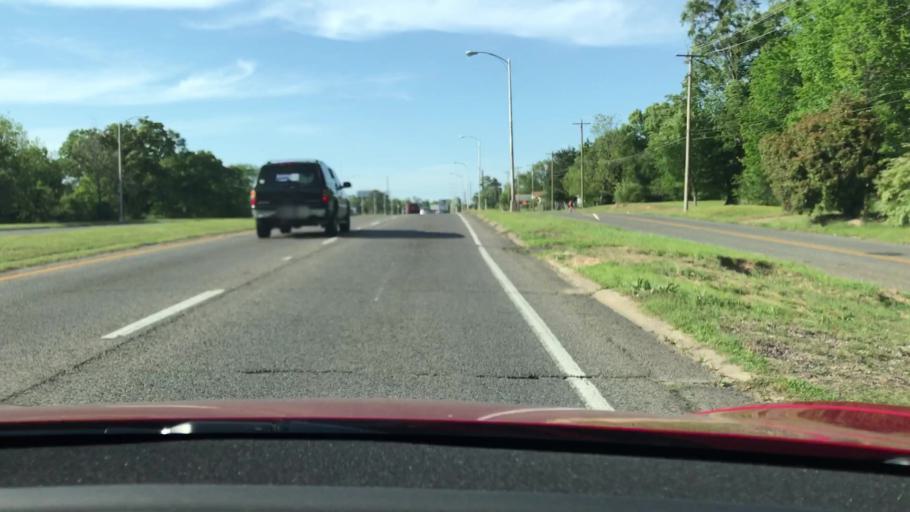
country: US
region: Louisiana
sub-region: Bossier Parish
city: Bossier City
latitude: 32.4945
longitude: -93.7247
